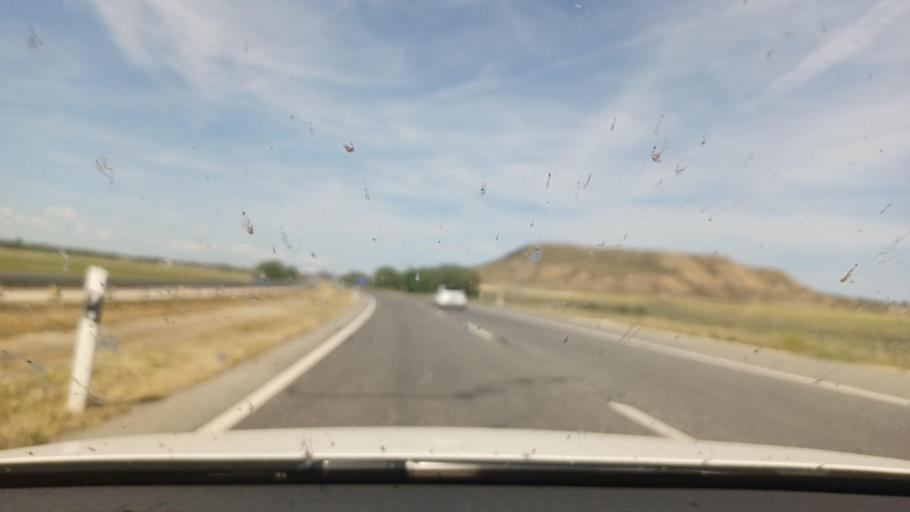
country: ES
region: Madrid
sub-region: Provincia de Madrid
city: Torrejon de Ardoz
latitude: 40.4403
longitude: -3.4284
